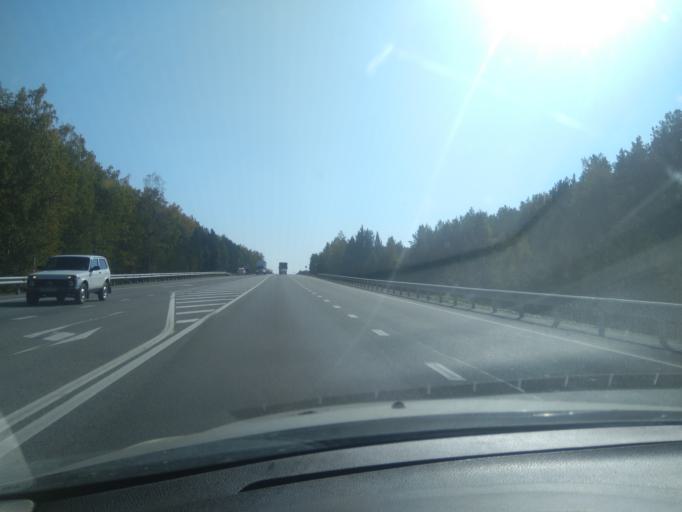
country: RU
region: Sverdlovsk
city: Verkhneye Dubrovo
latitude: 56.7191
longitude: 61.0525
